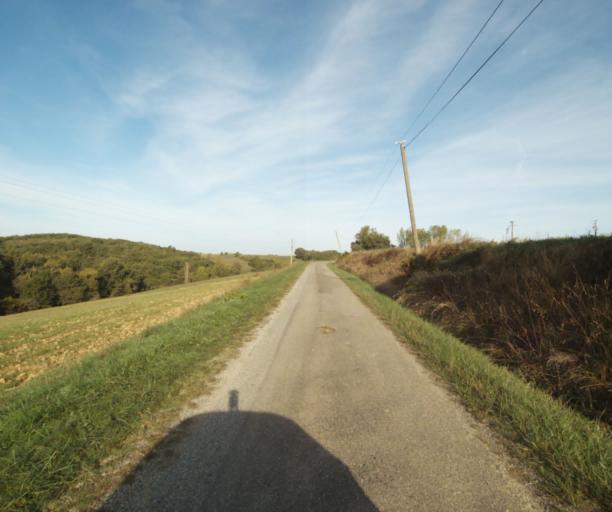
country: FR
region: Midi-Pyrenees
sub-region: Departement de la Haute-Garonne
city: Villemur-sur-Tarn
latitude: 43.9070
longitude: 1.5011
